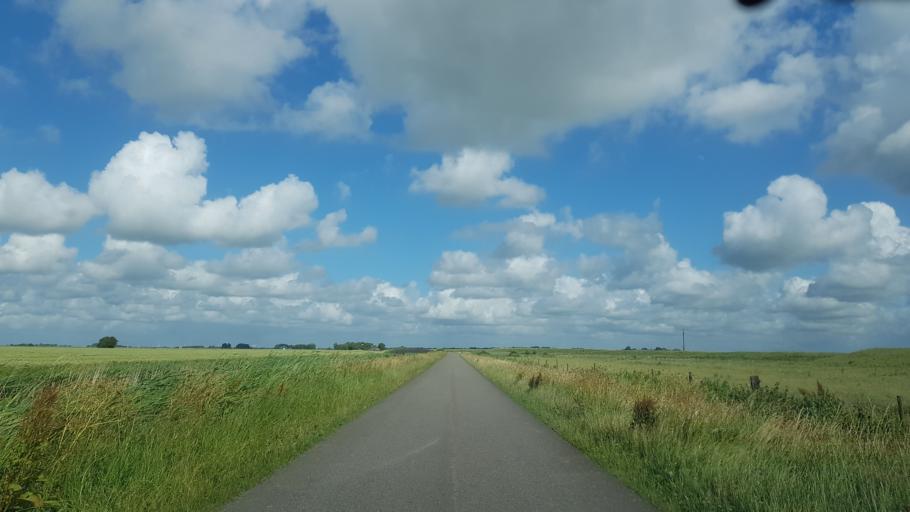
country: NL
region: Groningen
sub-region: Gemeente Winsum
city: Winsum
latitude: 53.4064
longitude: 6.5327
